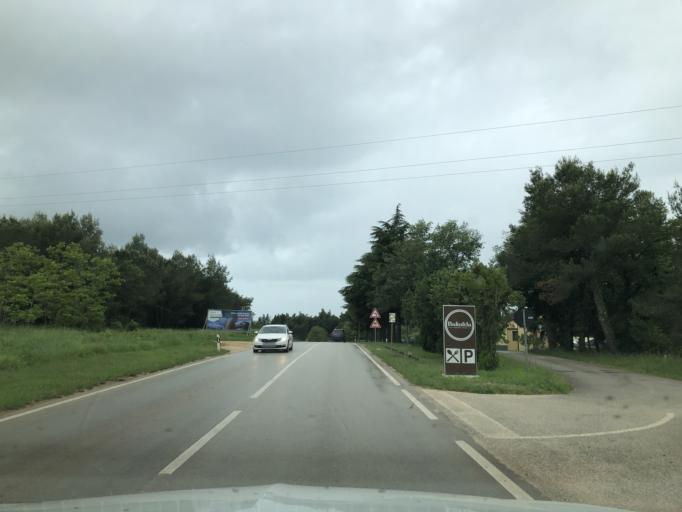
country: HR
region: Istarska
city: Umag
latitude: 45.4478
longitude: 13.5519
